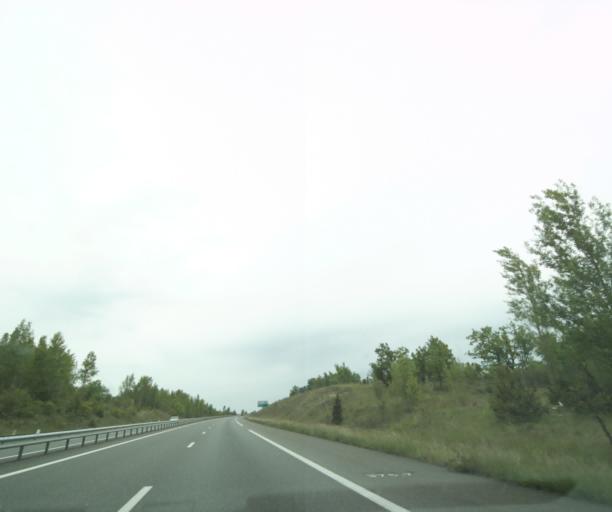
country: FR
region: Midi-Pyrenees
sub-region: Departement du Lot
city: Lalbenque
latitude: 44.3286
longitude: 1.5035
